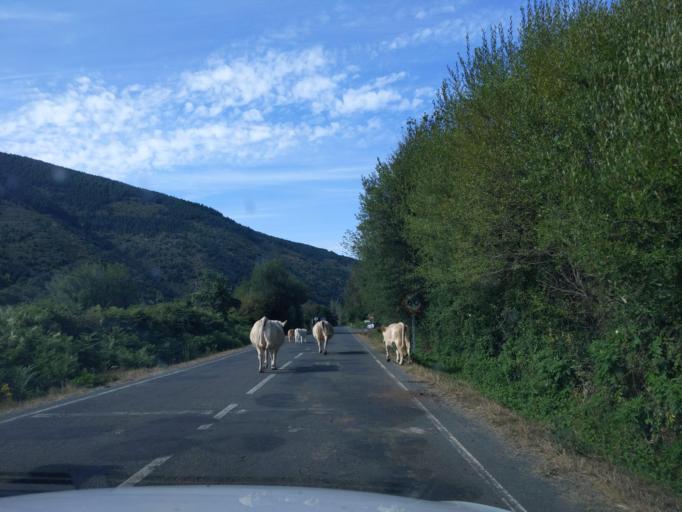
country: ES
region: La Rioja
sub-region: Provincia de La Rioja
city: Ezcaray
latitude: 42.2948
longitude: -3.0248
